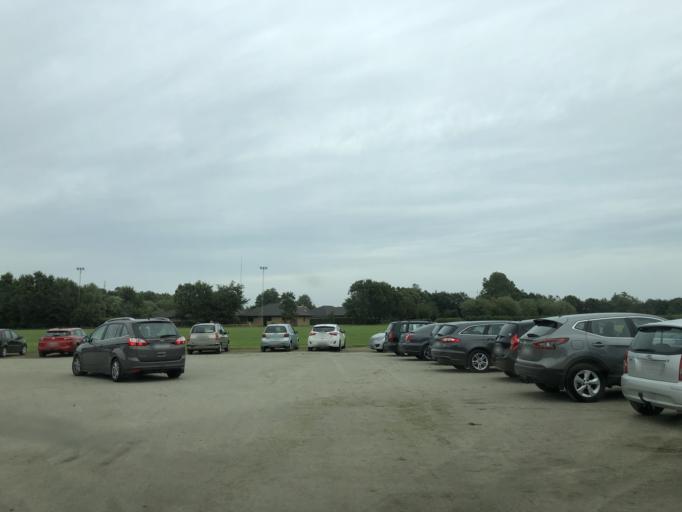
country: DK
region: North Denmark
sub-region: Morso Kommune
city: Nykobing Mors
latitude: 56.7981
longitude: 8.8511
